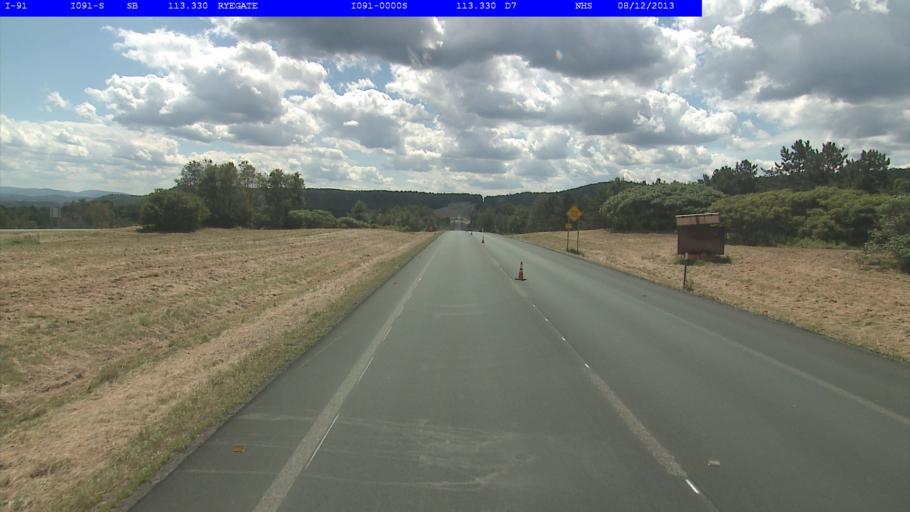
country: US
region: New Hampshire
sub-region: Grafton County
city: Woodsville
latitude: 44.2013
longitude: -72.0710
